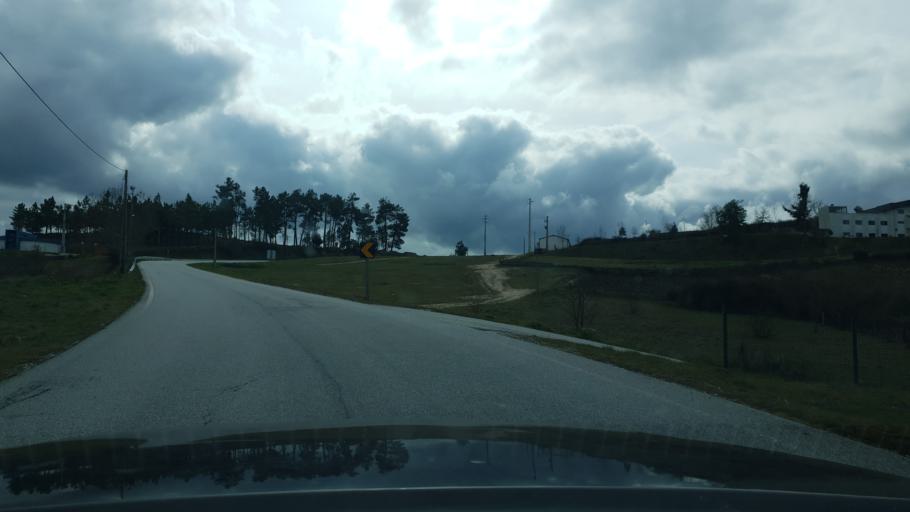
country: PT
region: Viseu
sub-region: Moimenta da Beira
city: Moimenta da Beira
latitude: 40.9566
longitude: -7.5830
